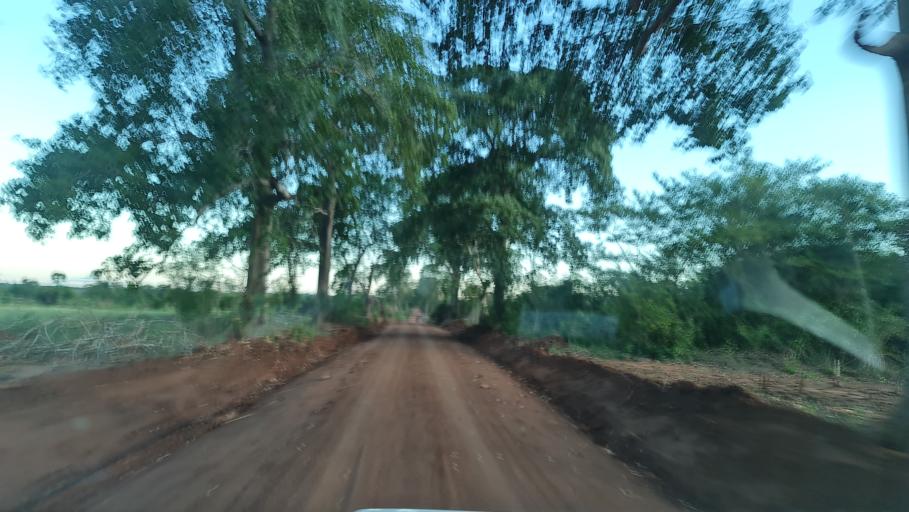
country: MZ
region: Nampula
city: Ilha de Mocambique
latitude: -14.9778
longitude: 40.0928
